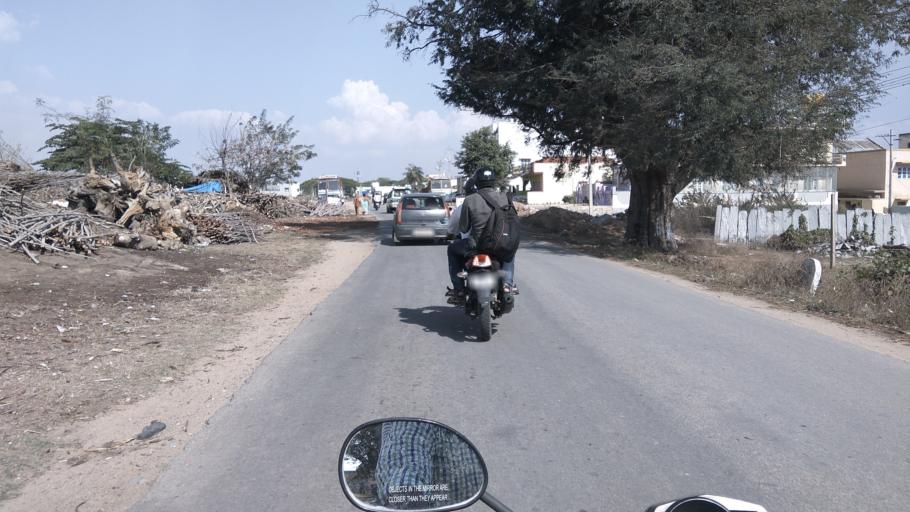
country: IN
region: Karnataka
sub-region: Kolar
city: Mulbagal
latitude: 13.1624
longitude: 78.3798
